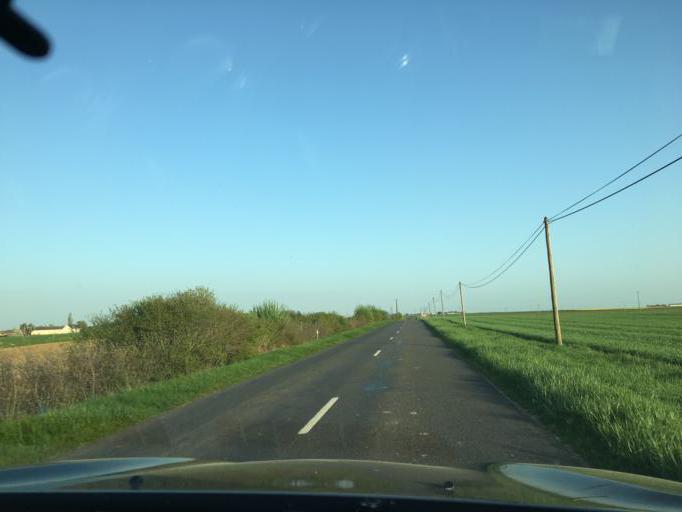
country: FR
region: Centre
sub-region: Departement du Loir-et-Cher
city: Ouzouer-le-Marche
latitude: 47.8471
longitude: 1.5309
